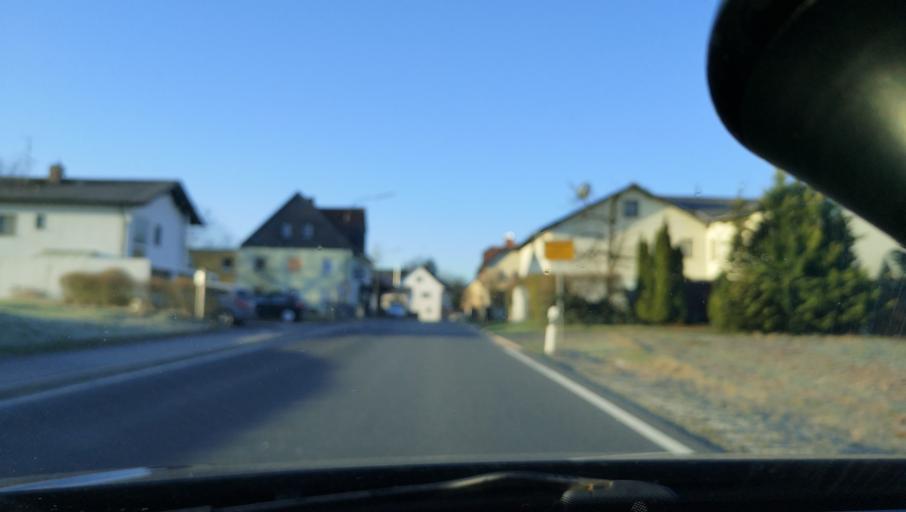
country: DE
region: Bavaria
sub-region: Upper Franconia
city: Sonnefeld
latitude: 50.2090
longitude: 11.1115
